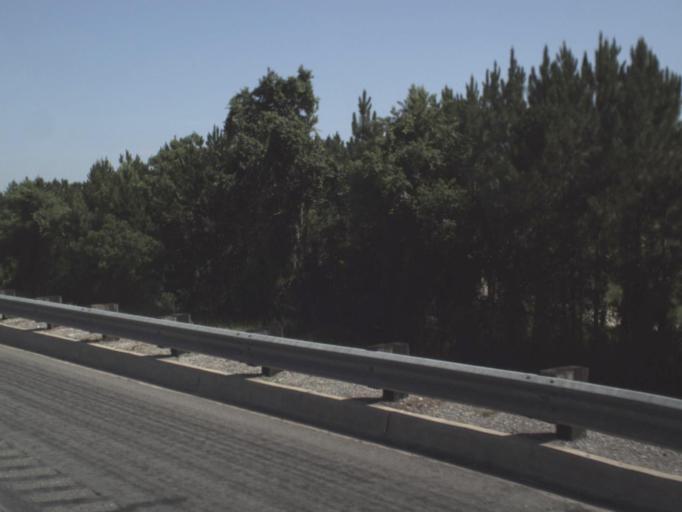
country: US
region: Florida
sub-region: Suwannee County
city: Live Oak
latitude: 30.3345
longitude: -82.9677
